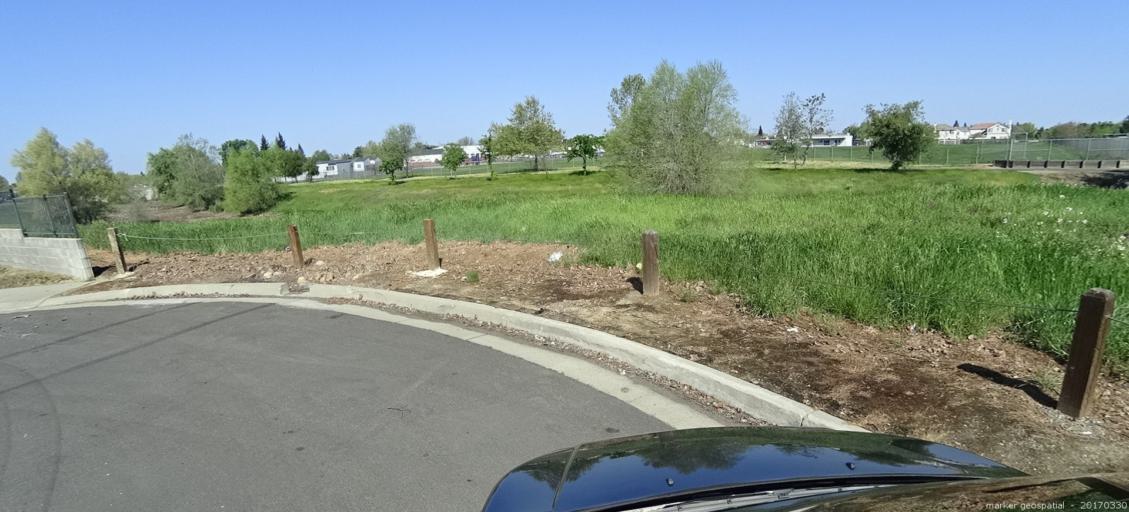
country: US
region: California
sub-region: Sacramento County
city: Laguna
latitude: 38.4430
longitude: -121.4088
